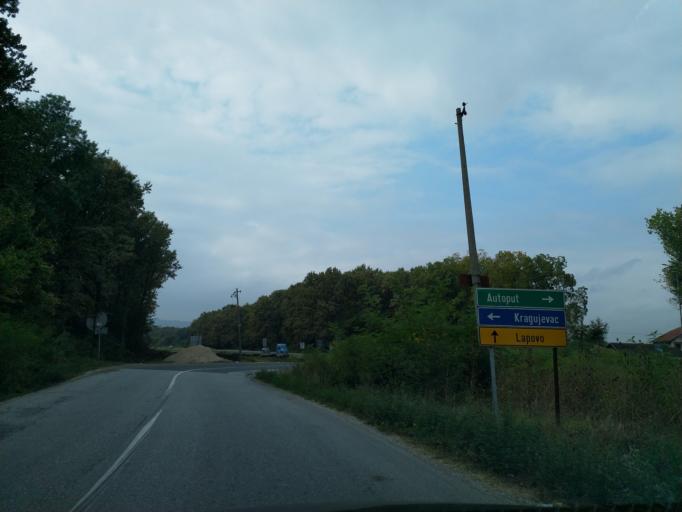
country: RS
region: Central Serbia
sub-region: Sumadijski Okrug
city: Batocina
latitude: 44.1483
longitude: 21.1077
